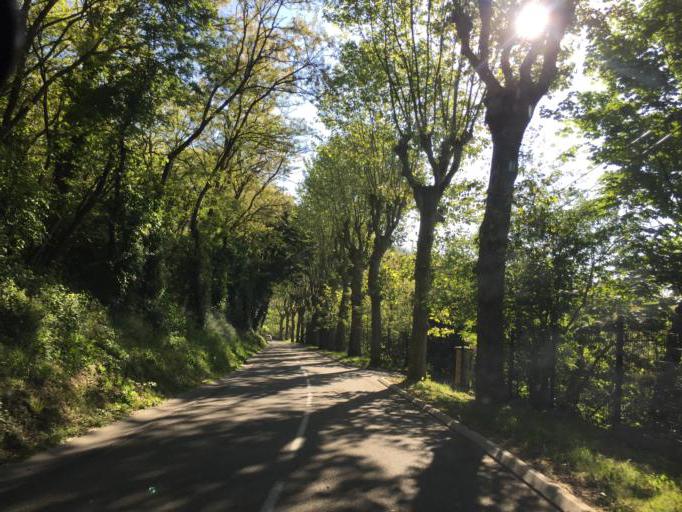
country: FR
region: Rhone-Alpes
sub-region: Departement de l'Ain
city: Beynost
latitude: 45.8426
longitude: 5.0000
